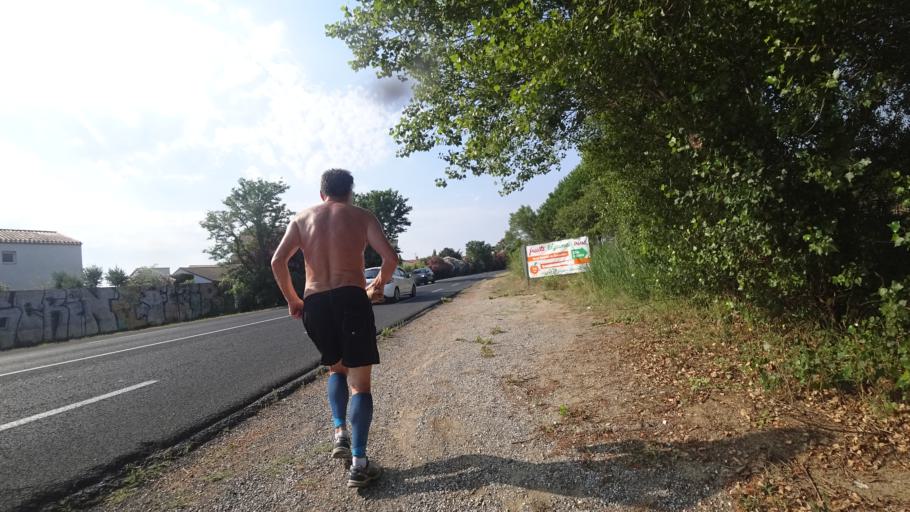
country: FR
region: Languedoc-Roussillon
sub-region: Departement des Pyrenees-Orientales
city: Canet-en-Roussillon
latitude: 42.6870
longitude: 3.0292
